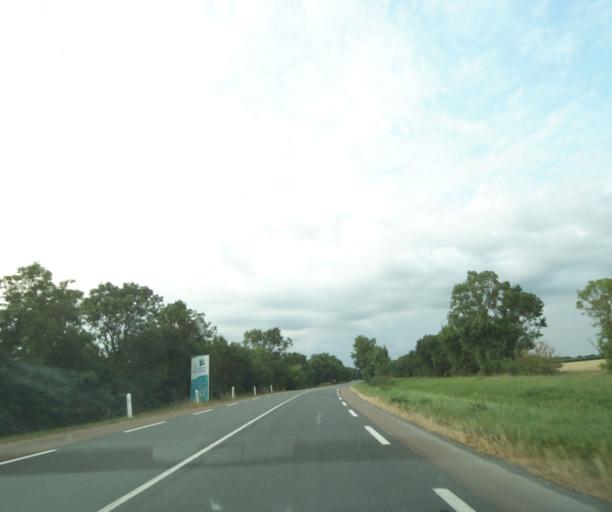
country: FR
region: Poitou-Charentes
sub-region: Departement de la Charente-Maritime
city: Marans
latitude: 46.3411
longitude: -0.9990
